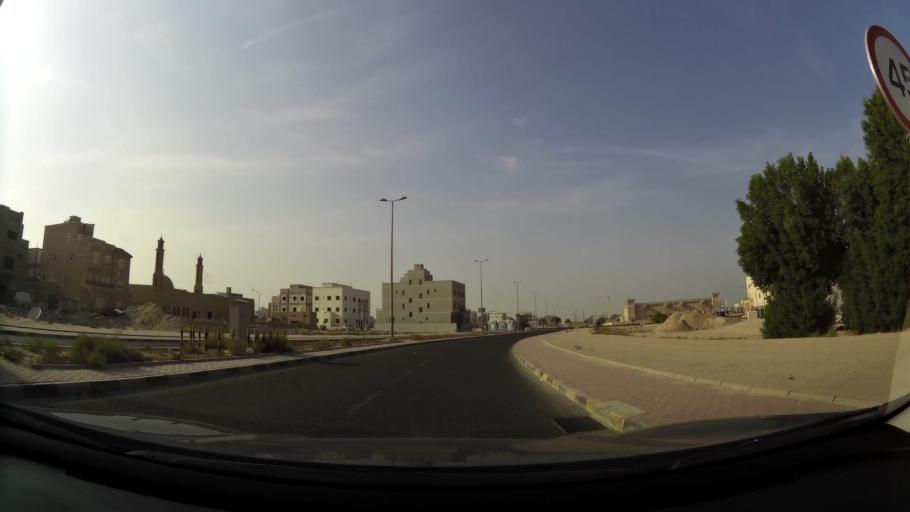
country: KW
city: Al Funaytis
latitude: 29.2086
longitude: 48.0984
